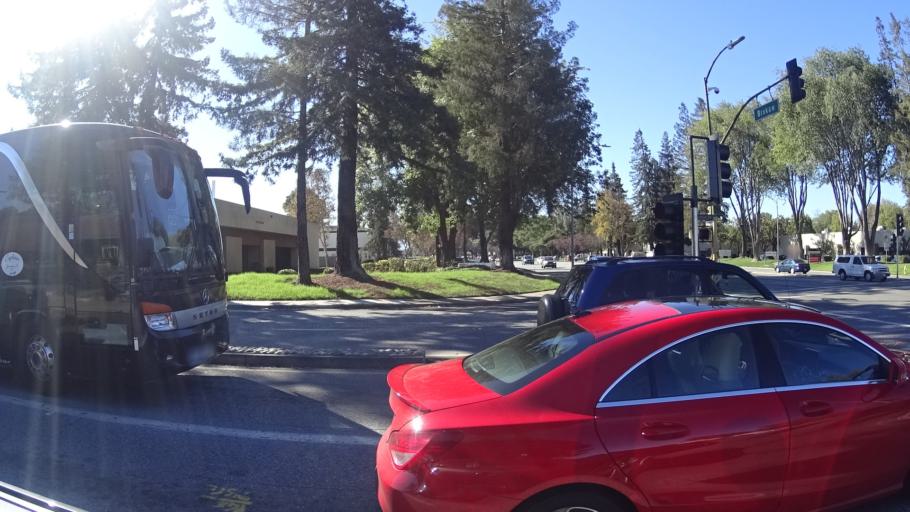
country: US
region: California
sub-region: Santa Clara County
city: San Jose
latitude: 37.3772
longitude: -121.9129
